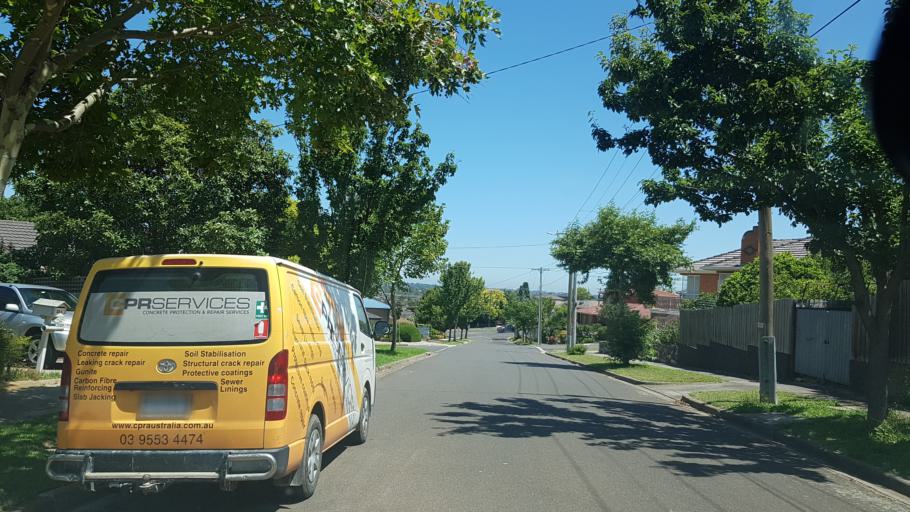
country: AU
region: Victoria
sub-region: Manningham
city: Bulleen
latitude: -37.7669
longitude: 145.0974
